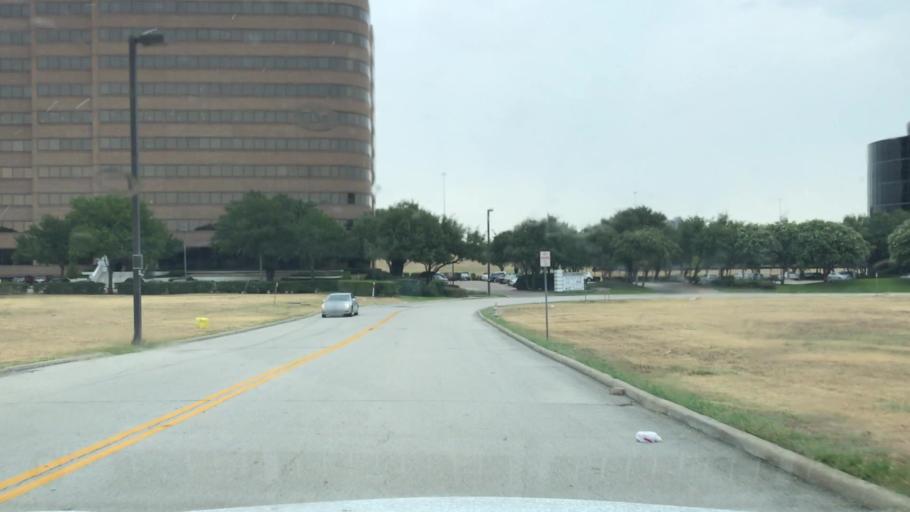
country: US
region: Texas
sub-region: Dallas County
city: Coppell
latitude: 32.8887
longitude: -96.9753
